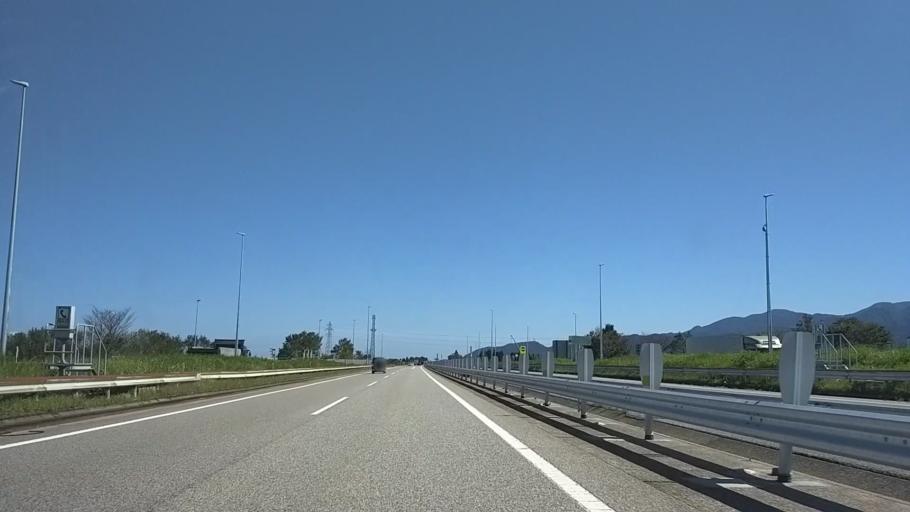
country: JP
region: Toyama
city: Nyuzen
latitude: 36.9162
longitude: 137.5132
